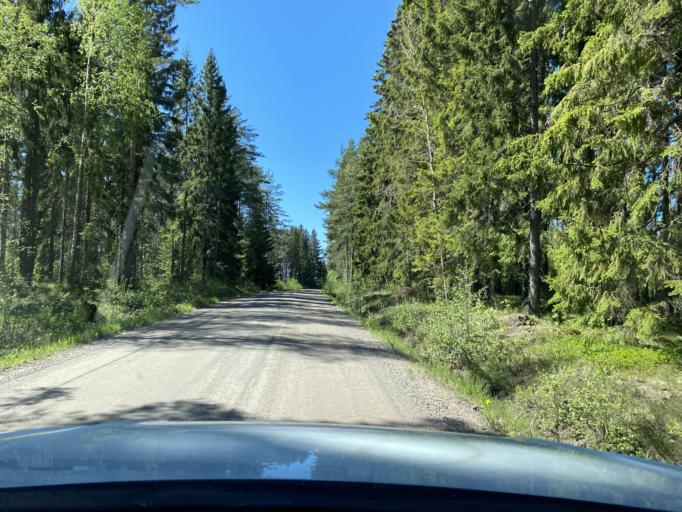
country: FI
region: Satakunta
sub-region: Rauma
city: Kiukainen
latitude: 61.1343
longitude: 21.9840
